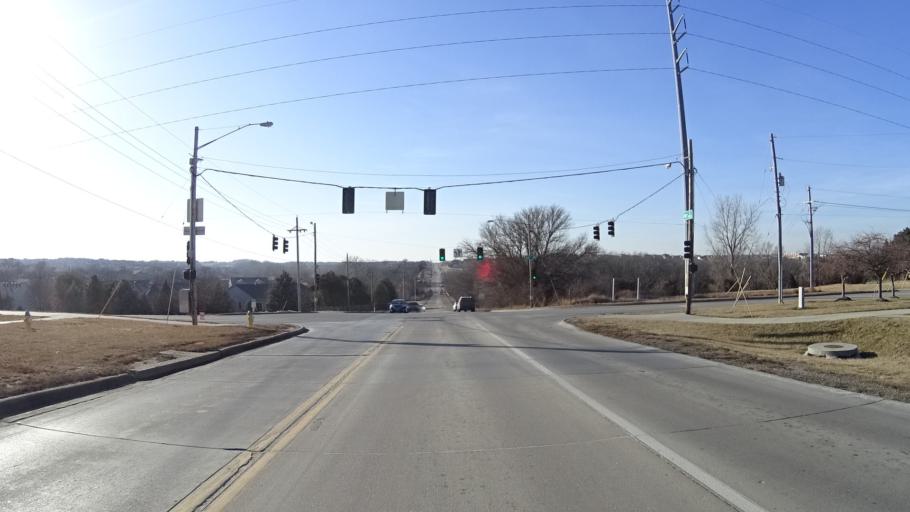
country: US
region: Nebraska
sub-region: Douglas County
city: Bennington
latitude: 41.3066
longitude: -96.1383
